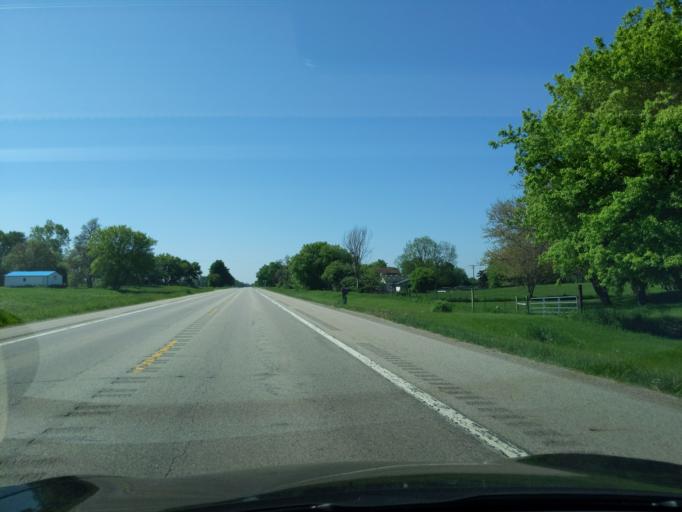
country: US
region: Michigan
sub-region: Ingham County
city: Stockbridge
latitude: 42.5312
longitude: -84.1909
